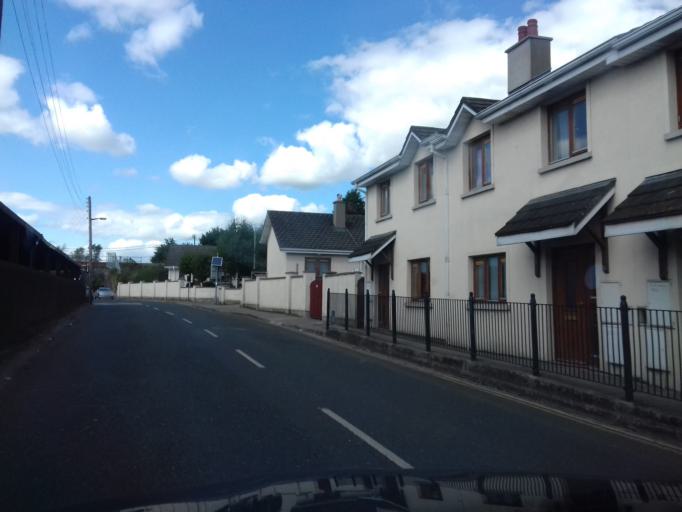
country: IE
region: Munster
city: Carrick-on-Suir
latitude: 52.3503
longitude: -7.4152
